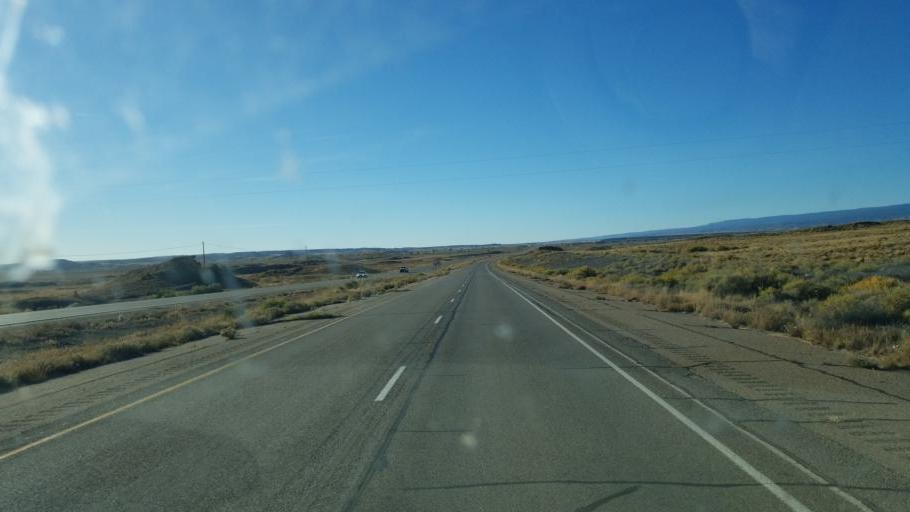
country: US
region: New Mexico
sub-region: San Juan County
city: Shiprock
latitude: 36.3256
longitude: -108.7102
